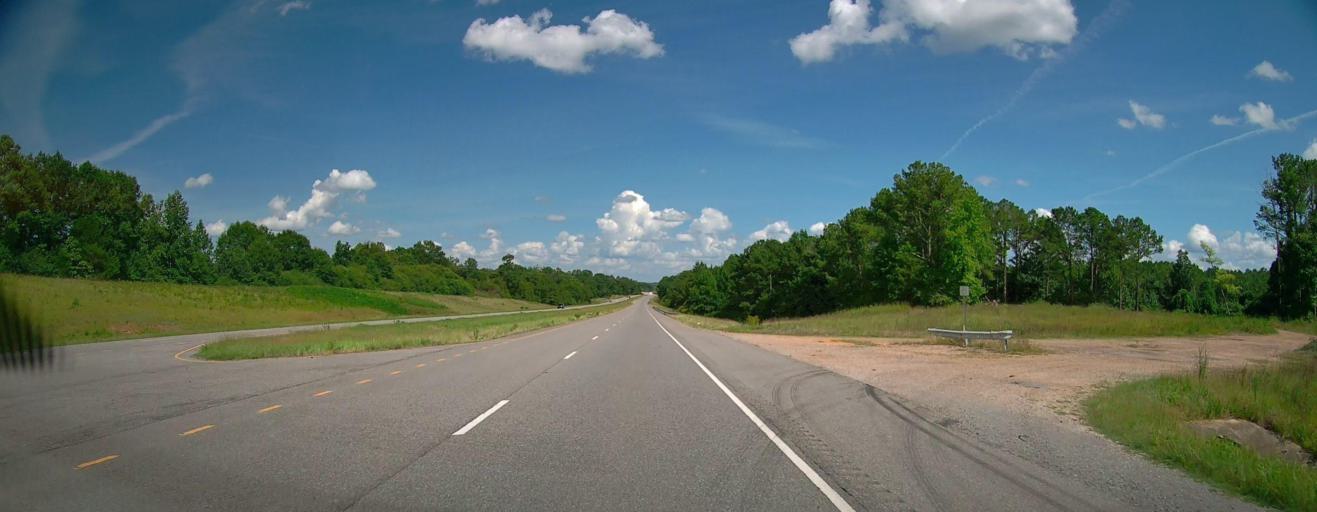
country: US
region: Alabama
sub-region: Pickens County
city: Reform
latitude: 33.3895
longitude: -88.0393
